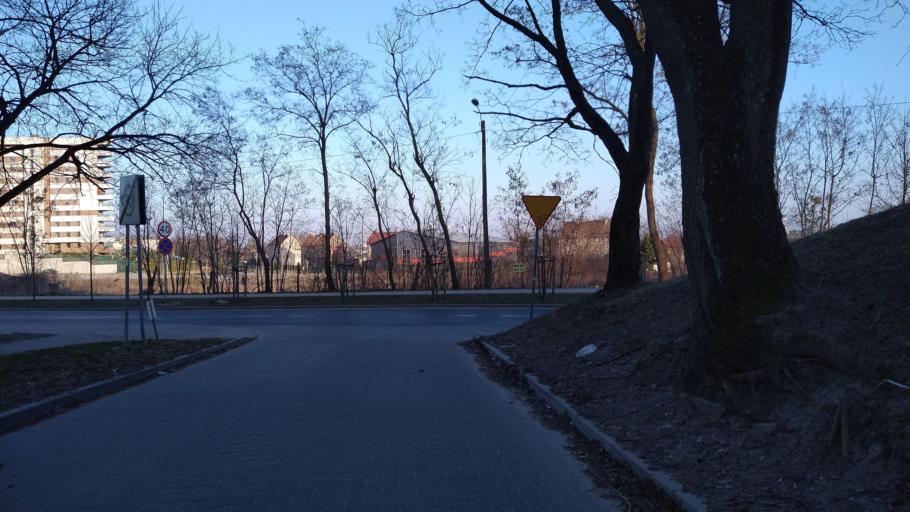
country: PL
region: Warmian-Masurian Voivodeship
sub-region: Powiat olsztynski
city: Olsztyn
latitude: 53.7903
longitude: 20.5021
